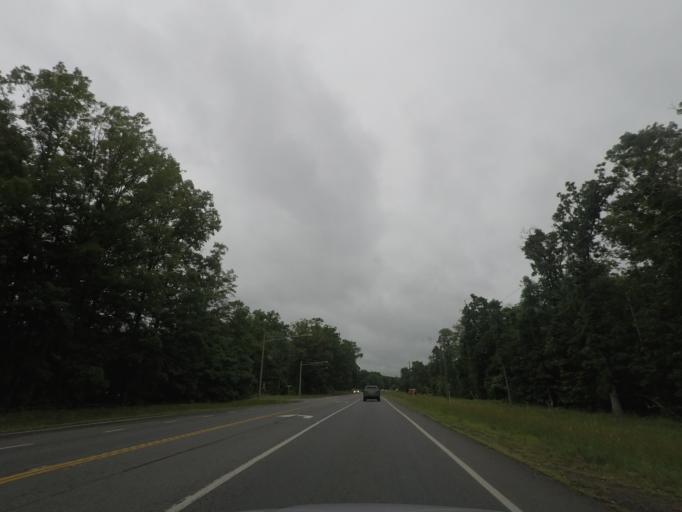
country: US
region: Virginia
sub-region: Prince William County
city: Haymarket
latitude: 38.7933
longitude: -77.6648
